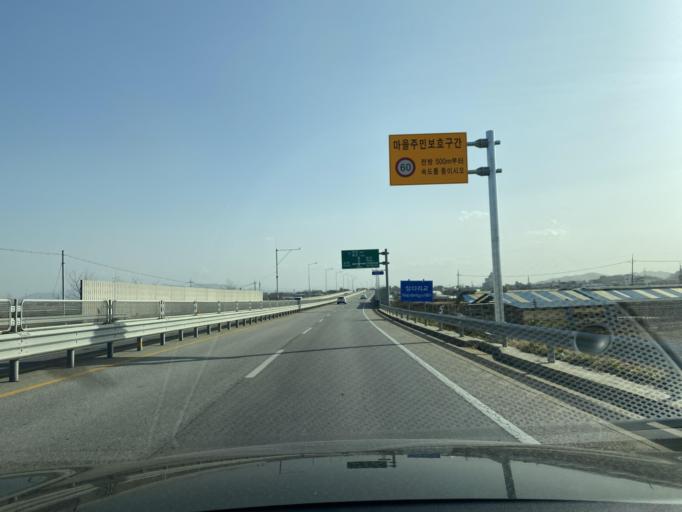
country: KR
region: Chungcheongnam-do
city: Yesan
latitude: 36.6923
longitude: 126.7325
